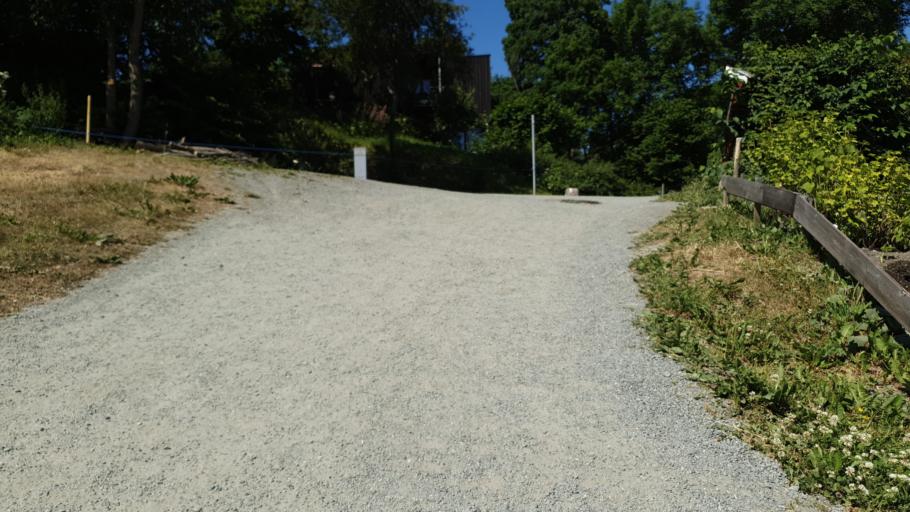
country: NO
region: Sor-Trondelag
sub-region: Trondheim
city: Trondheim
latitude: 63.4494
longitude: 10.4655
